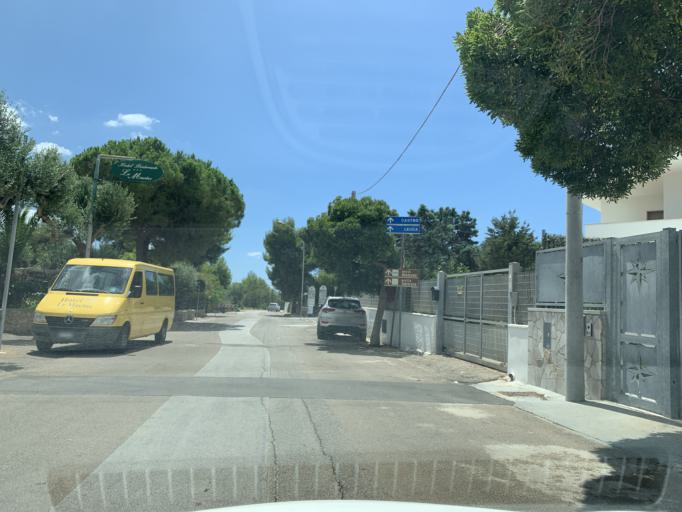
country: IT
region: Apulia
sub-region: Provincia di Lecce
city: Santa Cesarea Terme
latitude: 40.0345
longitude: 18.4522
